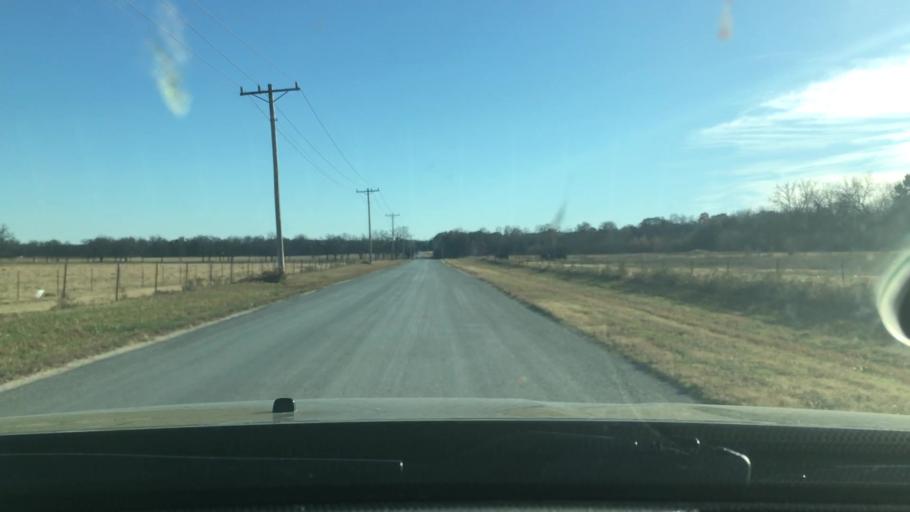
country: US
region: Oklahoma
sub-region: Murray County
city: Davis
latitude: 34.4969
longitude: -97.1583
